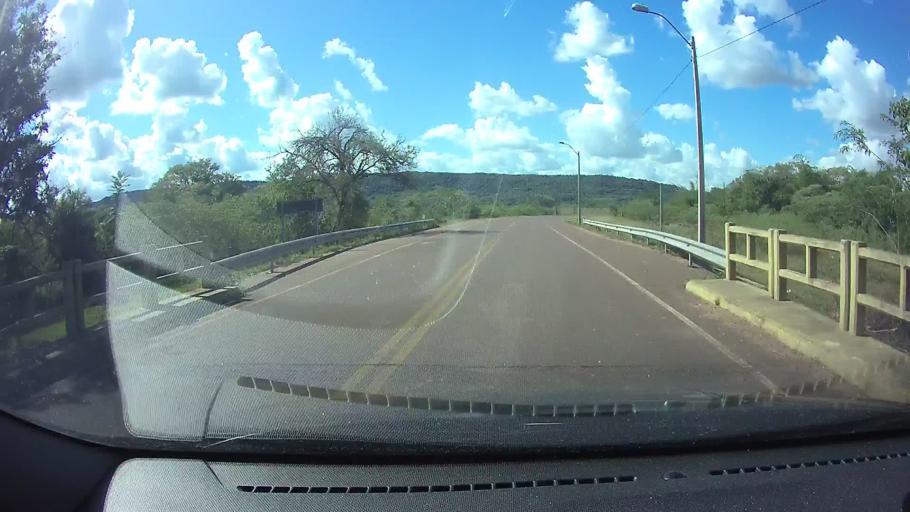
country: PY
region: Paraguari
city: Sapucai
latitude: -25.6853
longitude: -56.8635
